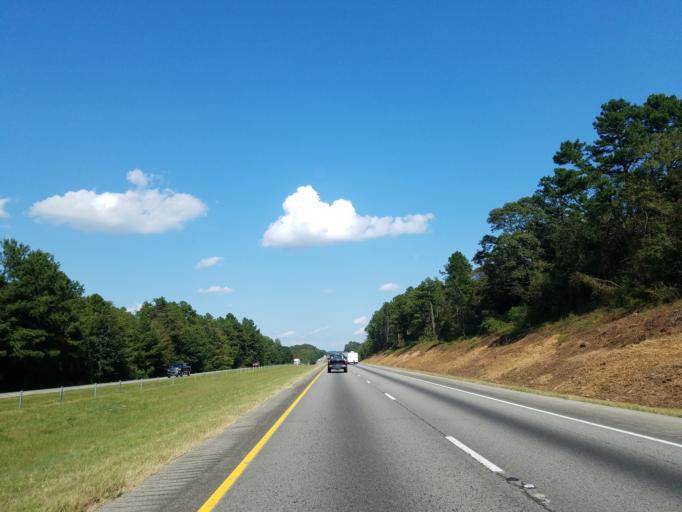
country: US
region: Georgia
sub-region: Banks County
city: Maysville
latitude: 34.1986
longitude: -83.5692
